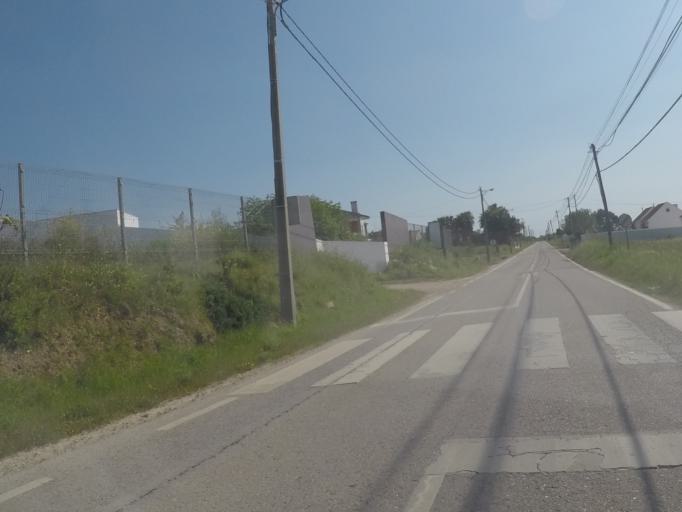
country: PT
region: Setubal
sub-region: Sesimbra
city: Sesimbra
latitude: 38.4393
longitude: -9.1755
